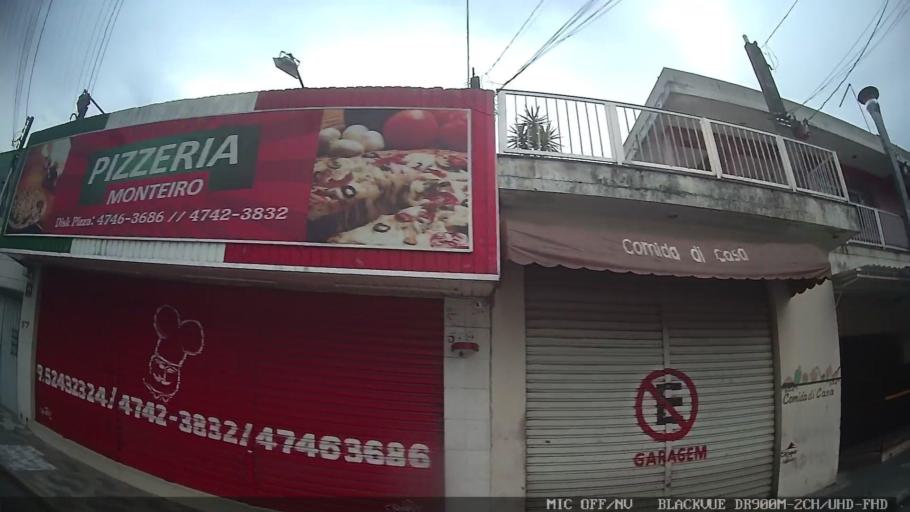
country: BR
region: Sao Paulo
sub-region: Suzano
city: Suzano
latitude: -23.5400
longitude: -46.3011
